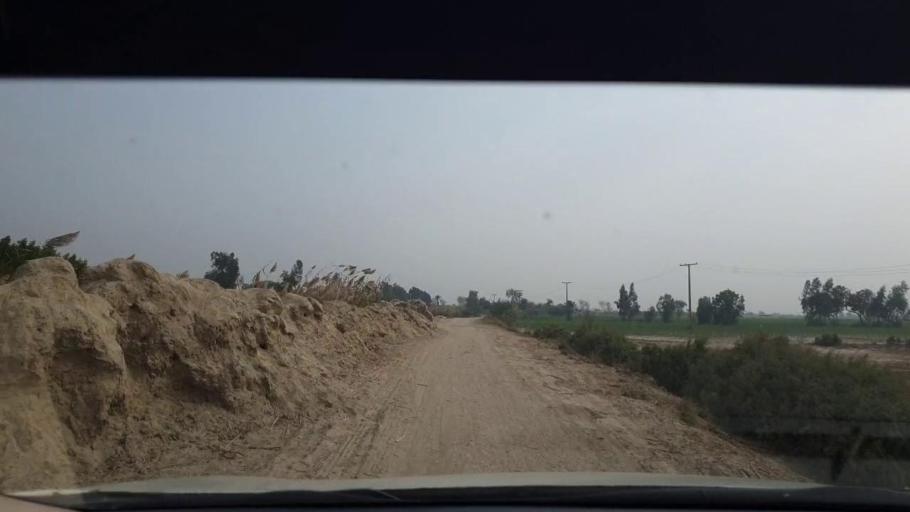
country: PK
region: Sindh
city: Berani
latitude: 25.8329
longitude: 68.8281
